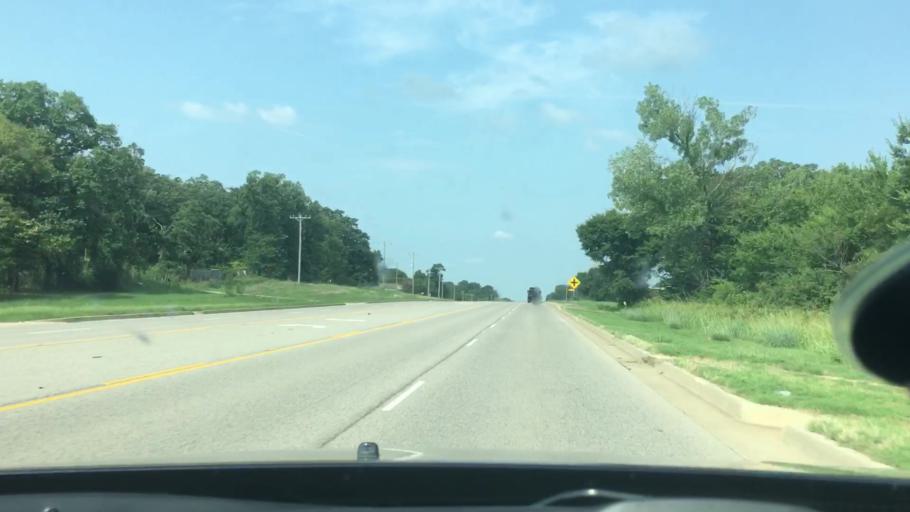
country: US
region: Oklahoma
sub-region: Bryan County
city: Calera
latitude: 33.9983
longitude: -96.5317
